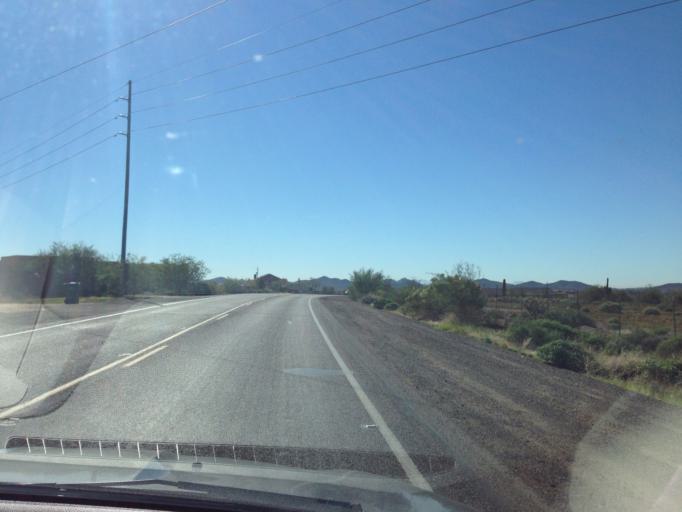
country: US
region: Arizona
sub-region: Maricopa County
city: Anthem
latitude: 33.8487
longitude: -112.0628
